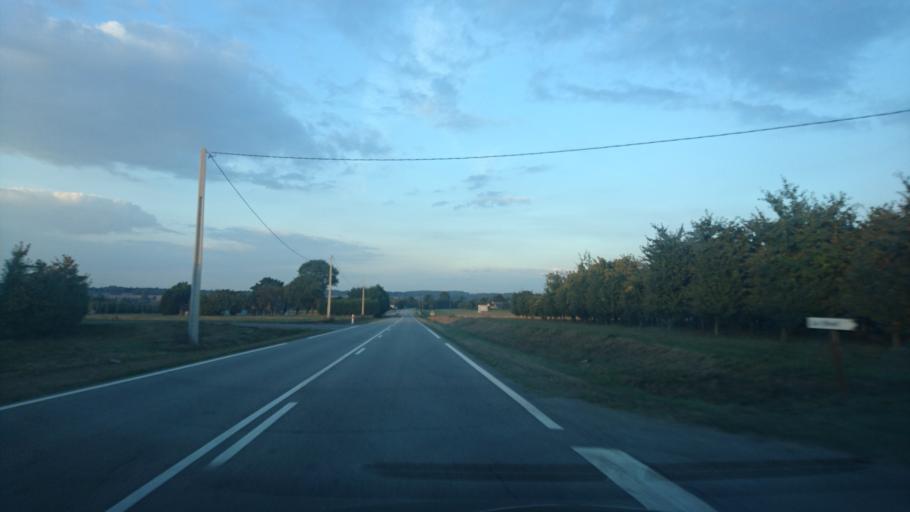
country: FR
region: Brittany
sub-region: Departement d'Ille-et-Vilaine
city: Maure-de-Bretagne
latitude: 47.9127
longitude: -1.9760
